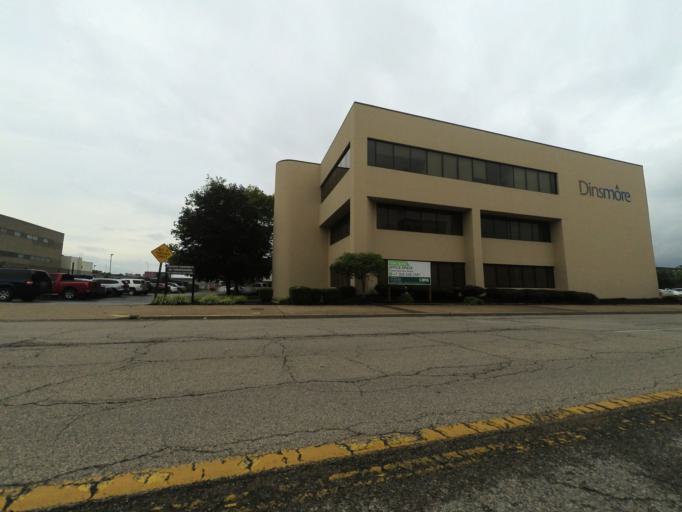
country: US
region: West Virginia
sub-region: Cabell County
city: Huntington
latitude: 38.4209
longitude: -82.4475
